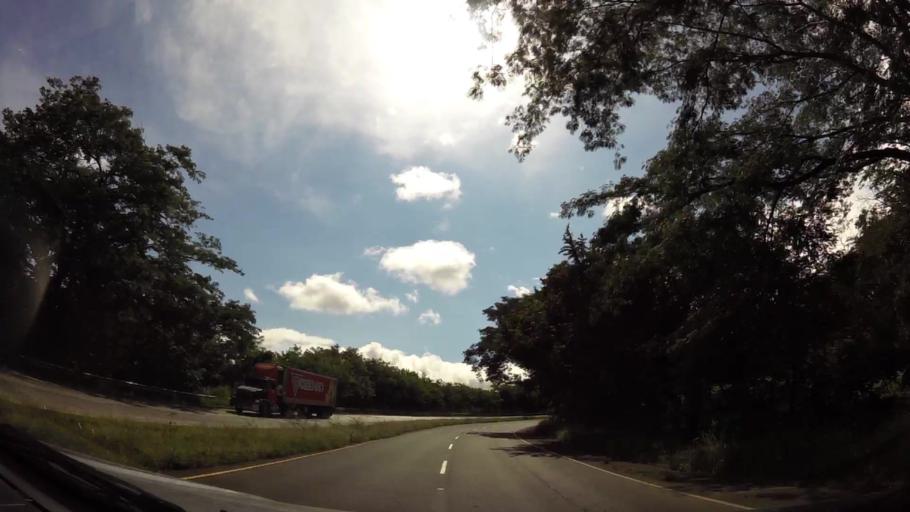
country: PA
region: Panama
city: Capira
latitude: 8.7085
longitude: -79.8729
